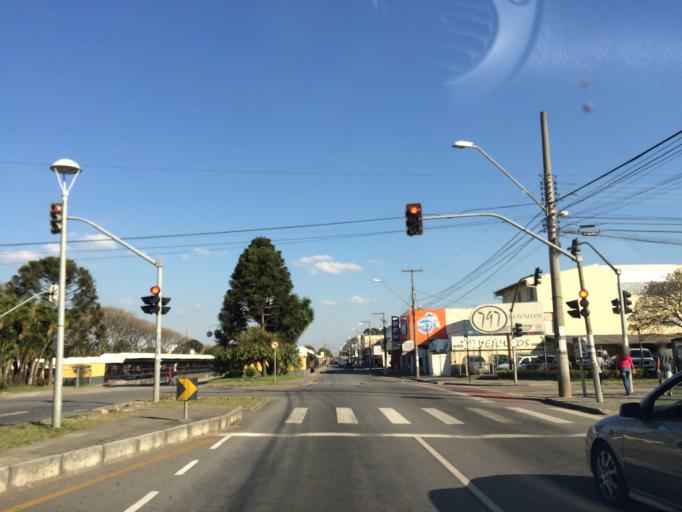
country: BR
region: Parana
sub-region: Curitiba
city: Curitiba
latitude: -25.4808
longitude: -49.2478
